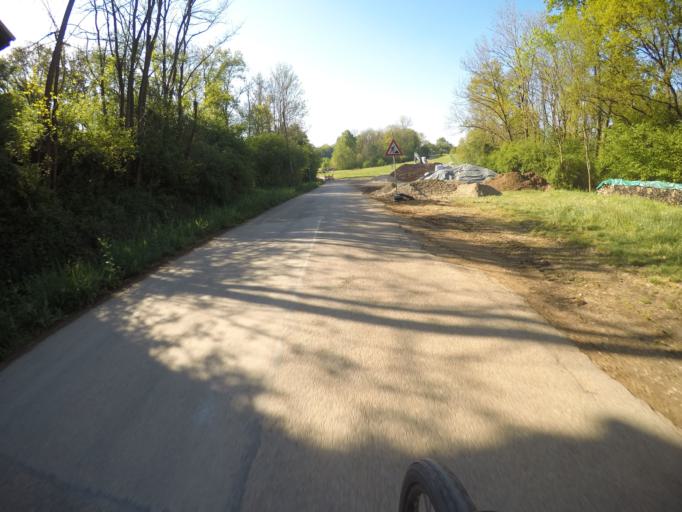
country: DE
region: Baden-Wuerttemberg
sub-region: Regierungsbezirk Stuttgart
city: Neckartailfingen
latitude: 48.6338
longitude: 9.2646
